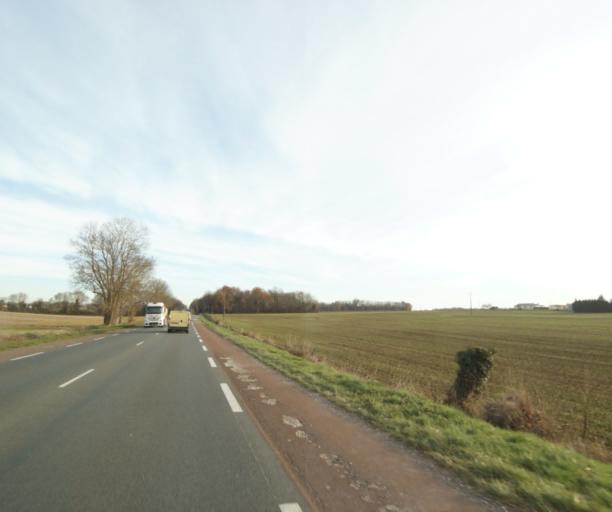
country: FR
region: Poitou-Charentes
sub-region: Departement de la Charente-Maritime
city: Saint-Georges-des-Coteaux
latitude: 45.7834
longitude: -0.7115
